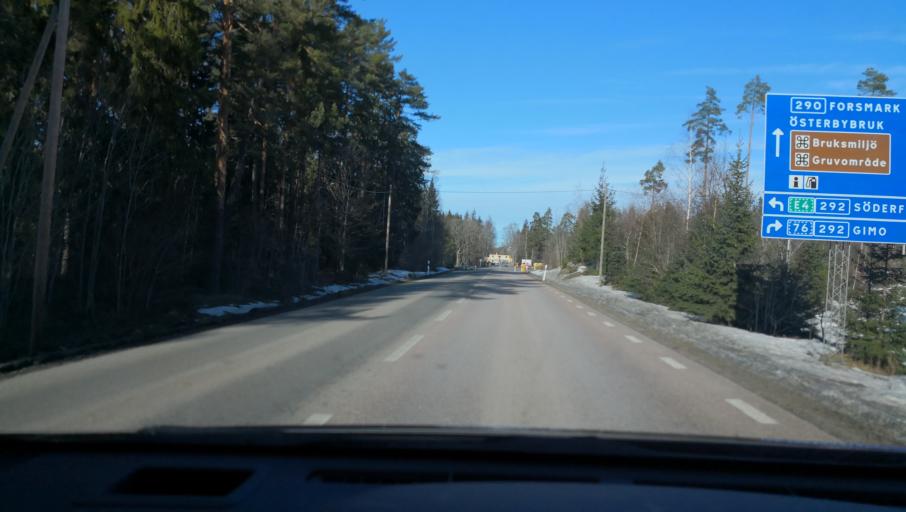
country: SE
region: Uppsala
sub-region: Osthammars Kommun
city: Osterbybruk
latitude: 60.1927
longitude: 17.8777
